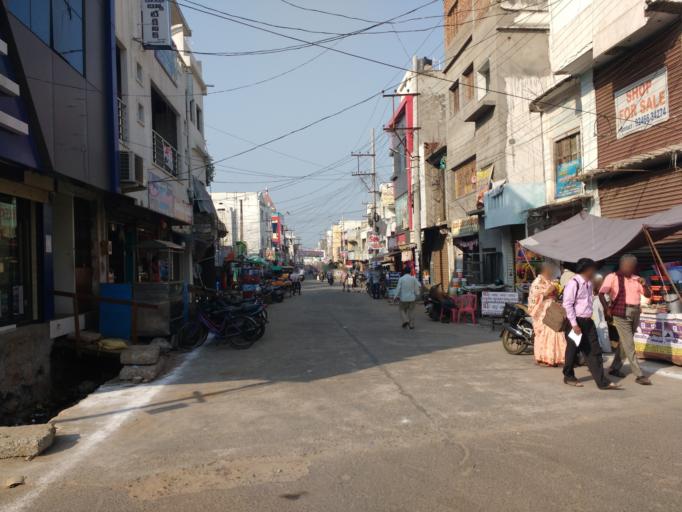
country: IN
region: Andhra Pradesh
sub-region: Srikakulam
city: Srikakulam
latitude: 18.2950
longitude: 83.8966
